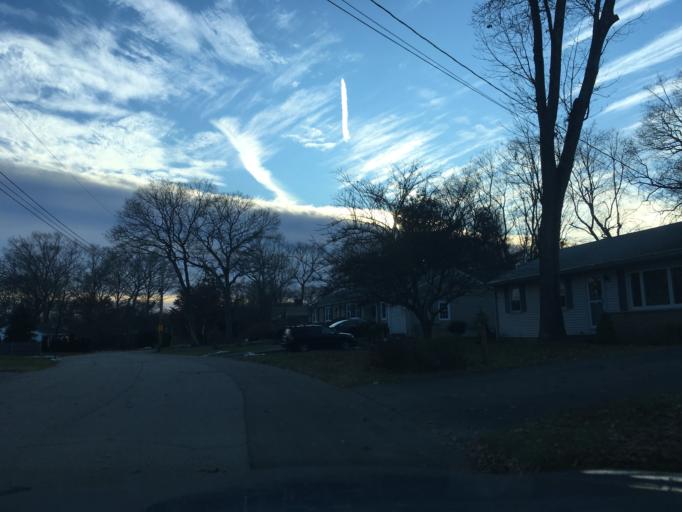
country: US
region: Rhode Island
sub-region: Kent County
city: East Greenwich
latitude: 41.6474
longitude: -71.4669
